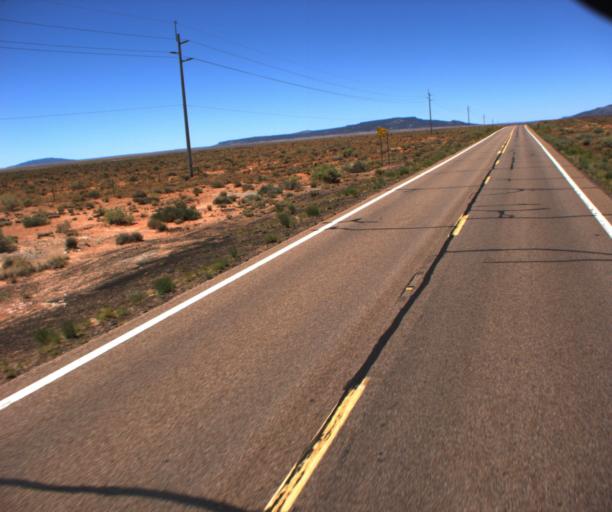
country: US
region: Arizona
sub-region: Coconino County
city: LeChee
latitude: 34.9423
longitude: -110.7770
